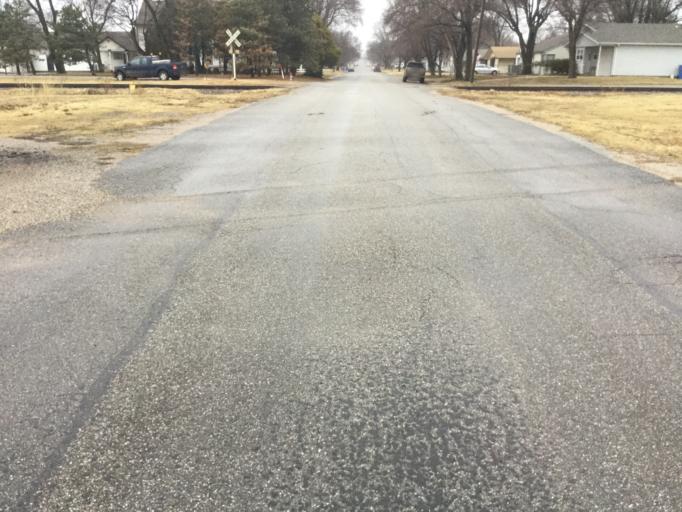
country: US
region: Kansas
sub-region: Sedgwick County
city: Cheney
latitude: 37.6267
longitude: -97.7782
